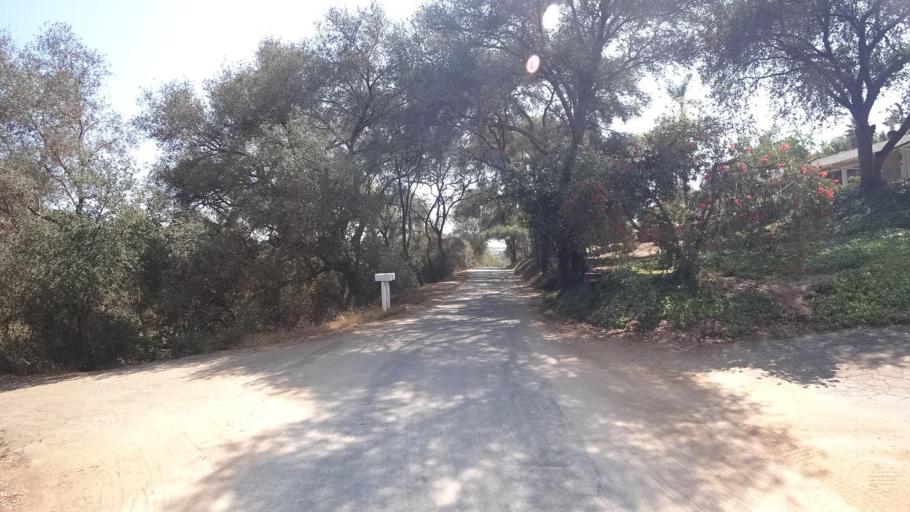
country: US
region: California
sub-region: San Diego County
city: Bonsall
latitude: 33.2879
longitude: -117.2564
